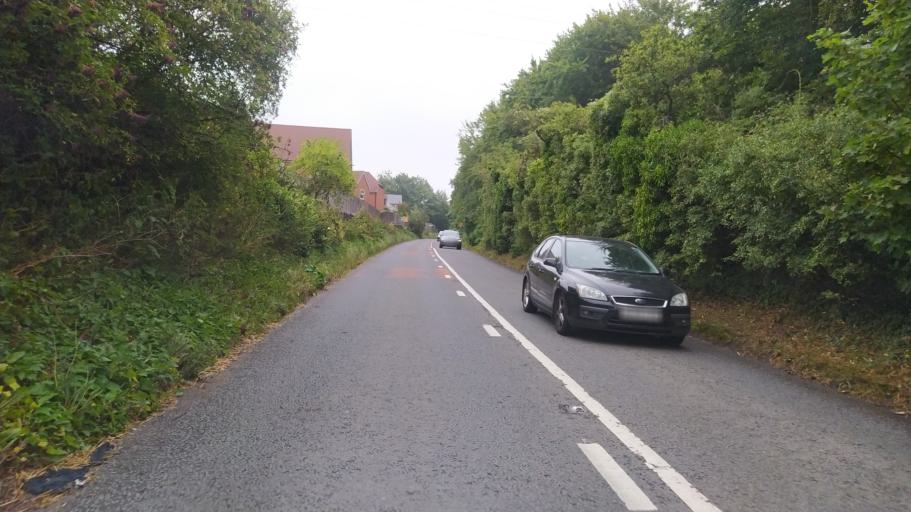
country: GB
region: England
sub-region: Wiltshire
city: Salisbury
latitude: 51.0531
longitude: -1.8125
